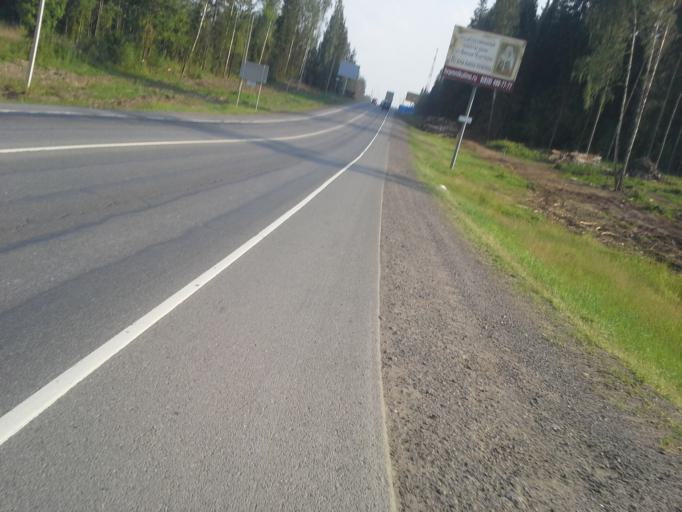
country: RU
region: Moskovskaya
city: Yershovo
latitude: 55.8345
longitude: 36.9213
